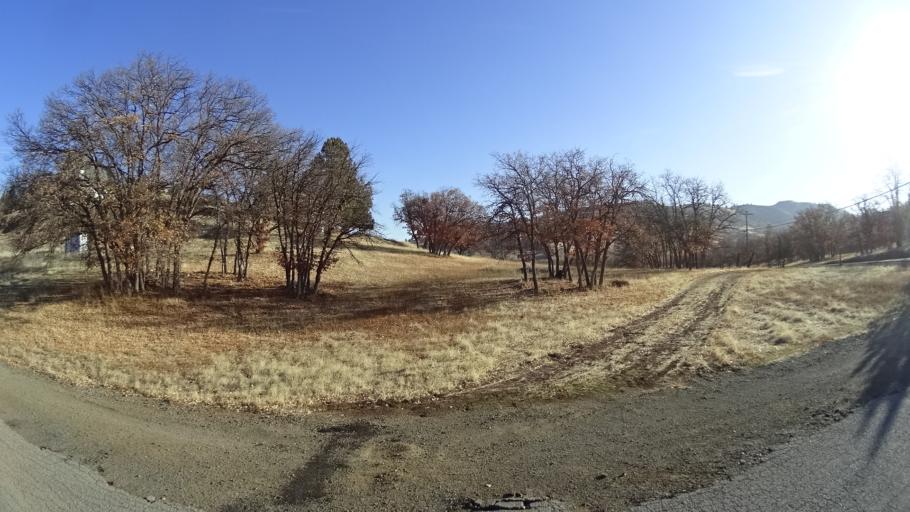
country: US
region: California
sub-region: Siskiyou County
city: Montague
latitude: 41.8885
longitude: -122.4881
